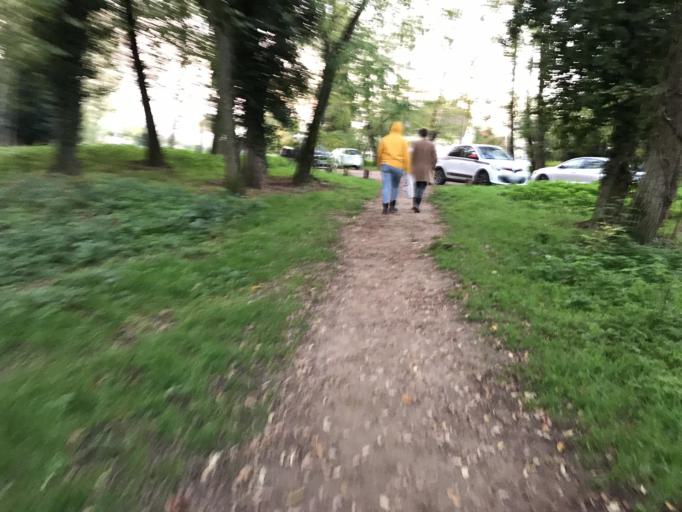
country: FR
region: Ile-de-France
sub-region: Departement de l'Essonne
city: Saulx-les-Chartreux
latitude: 48.6741
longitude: 2.2694
